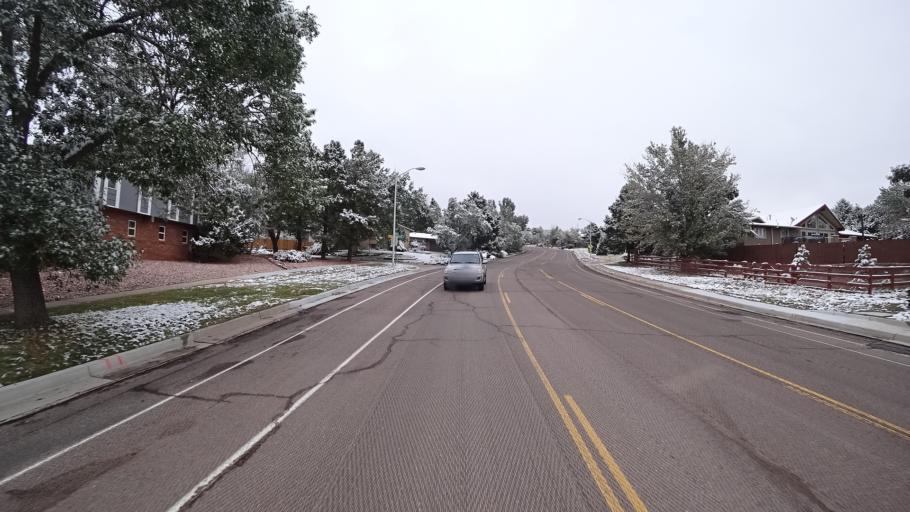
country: US
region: Colorado
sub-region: El Paso County
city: Cimarron Hills
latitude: 38.9114
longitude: -104.7608
